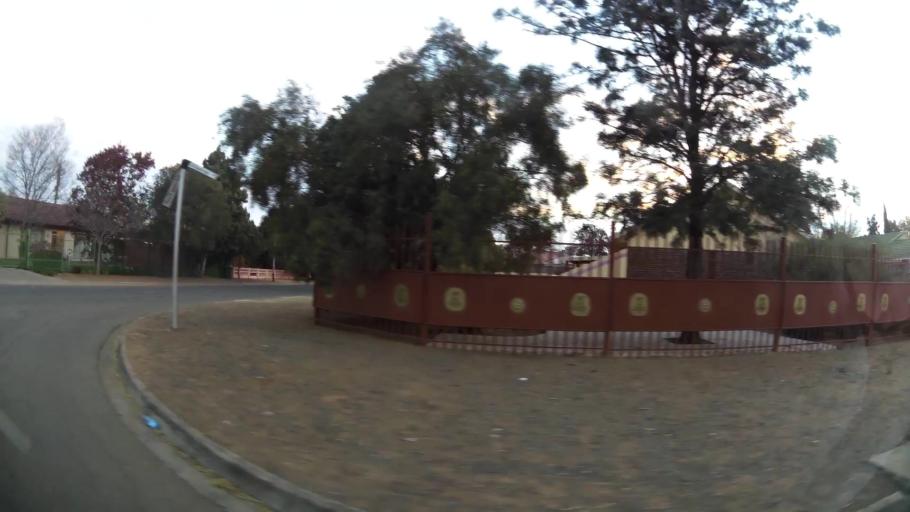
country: ZA
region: Orange Free State
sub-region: Mangaung Metropolitan Municipality
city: Bloemfontein
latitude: -29.1682
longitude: 26.1893
